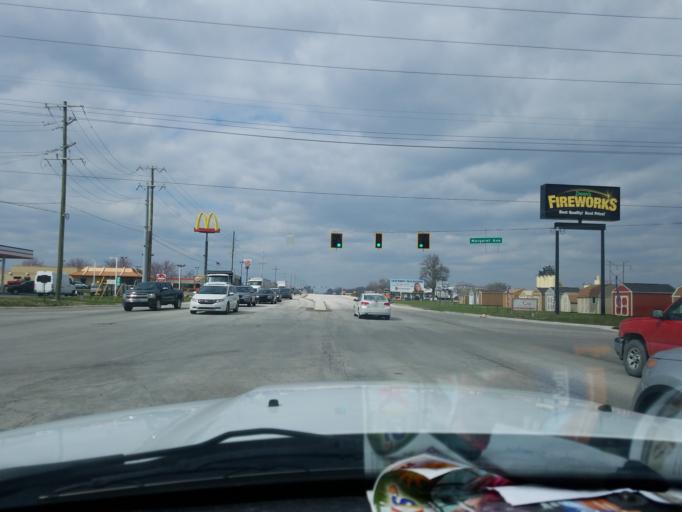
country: US
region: Indiana
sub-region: Vigo County
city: Terre Haute
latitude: 39.4336
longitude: -87.3329
